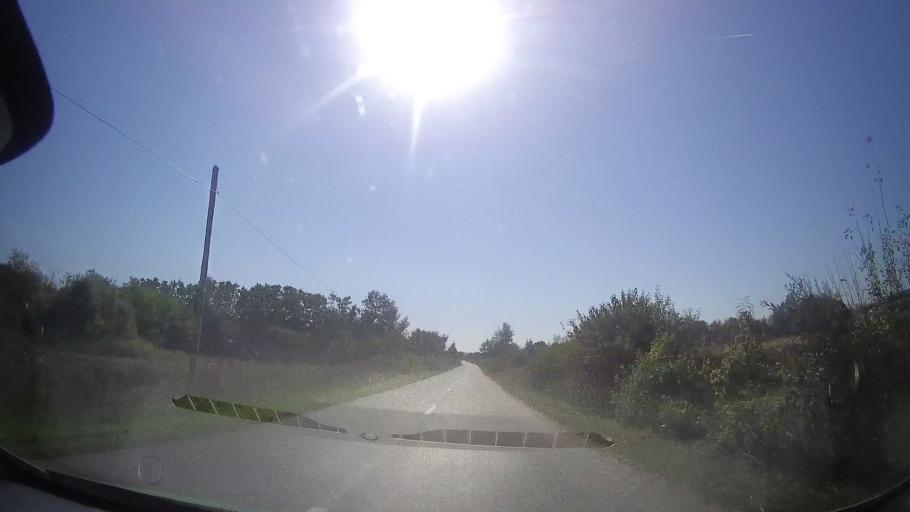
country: RO
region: Timis
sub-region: Comuna Ohaba Lunga
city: Ohaba Lunga
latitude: 45.8768
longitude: 21.9646
